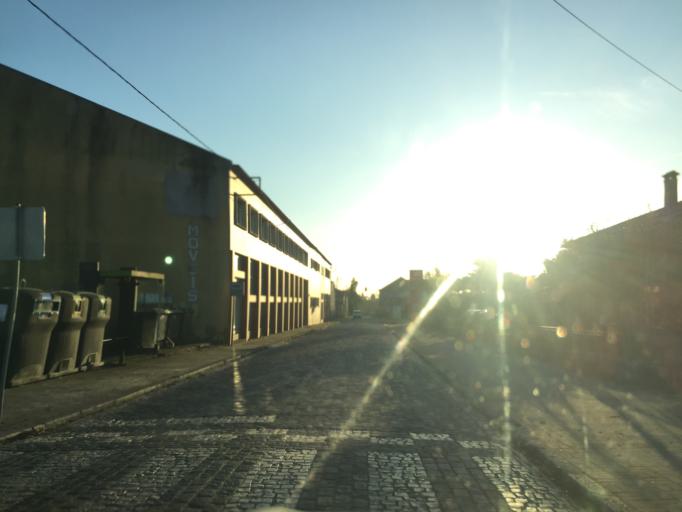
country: PT
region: Viseu
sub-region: Concelho de Carregal do Sal
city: Carregal do Sal
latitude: 40.4476
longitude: -7.9674
